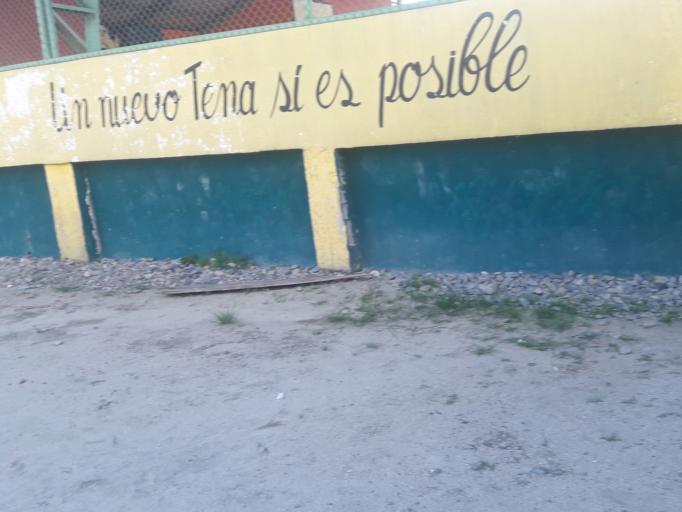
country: EC
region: Napo
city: Tena
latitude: -1.0042
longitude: -77.8133
